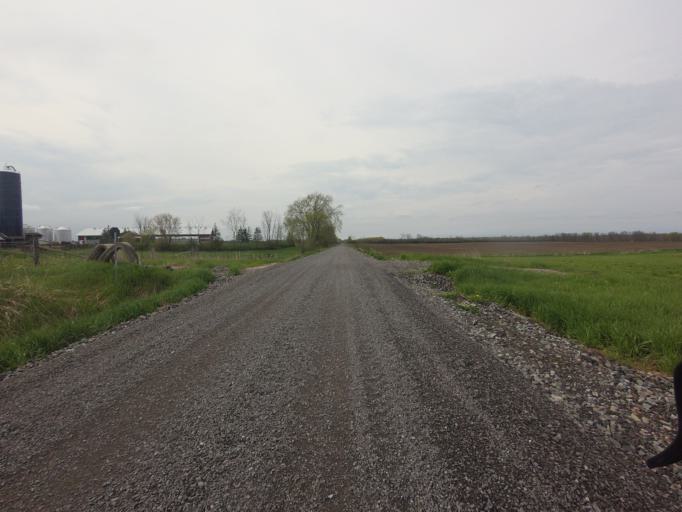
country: CA
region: Ontario
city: Carleton Place
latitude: 45.1905
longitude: -76.1619
